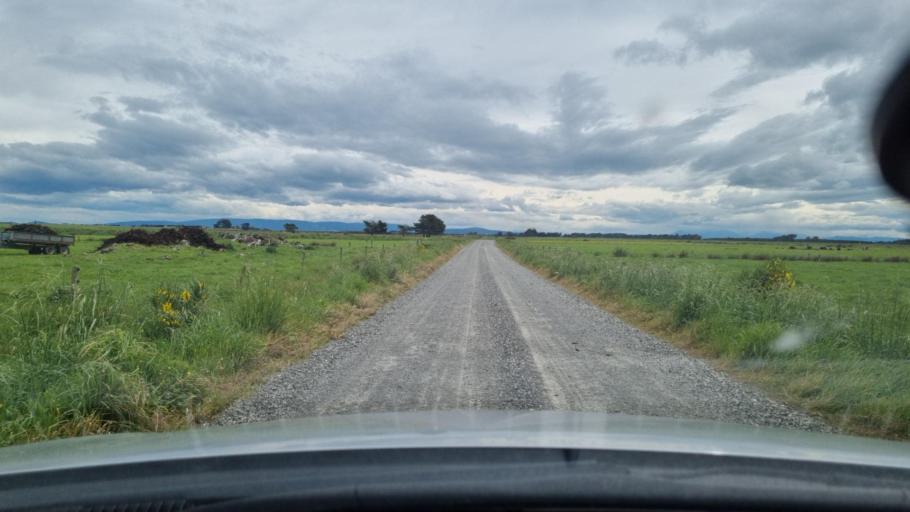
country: NZ
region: Southland
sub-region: Invercargill City
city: Invercargill
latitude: -46.4025
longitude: 168.2858
